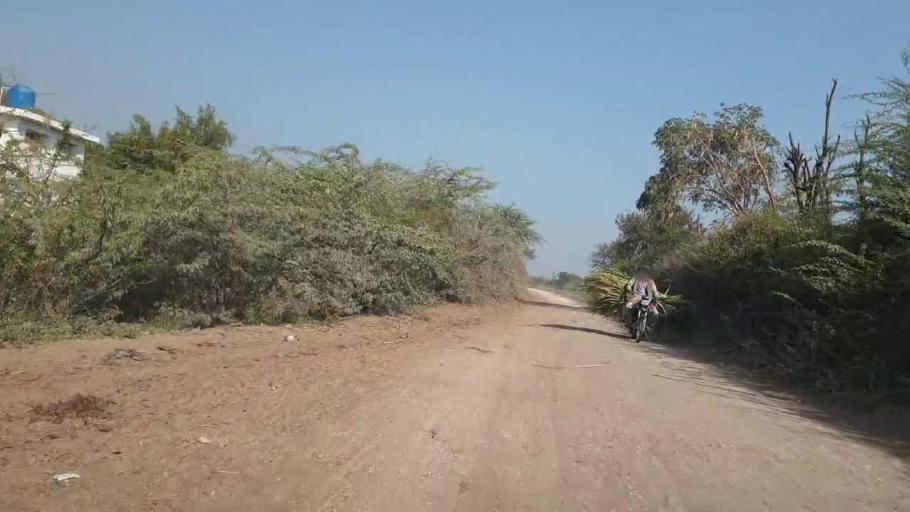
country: PK
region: Sindh
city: Tando Allahyar
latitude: 25.5906
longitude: 68.7481
